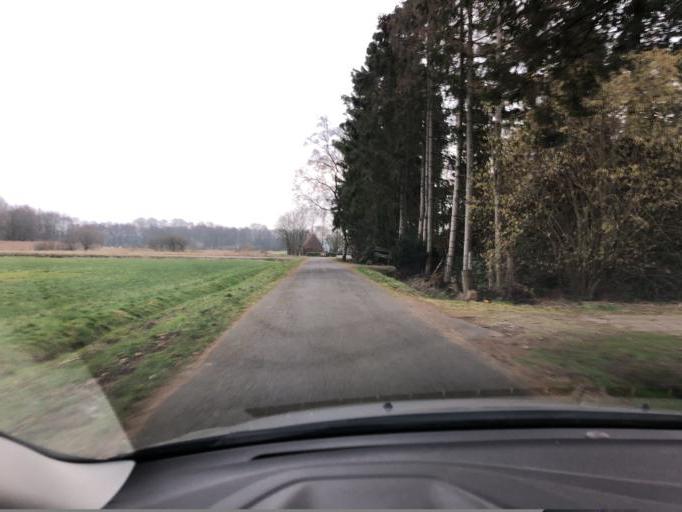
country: DE
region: Lower Saxony
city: Bad Zwischenahn
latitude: 53.1716
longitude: 8.0137
